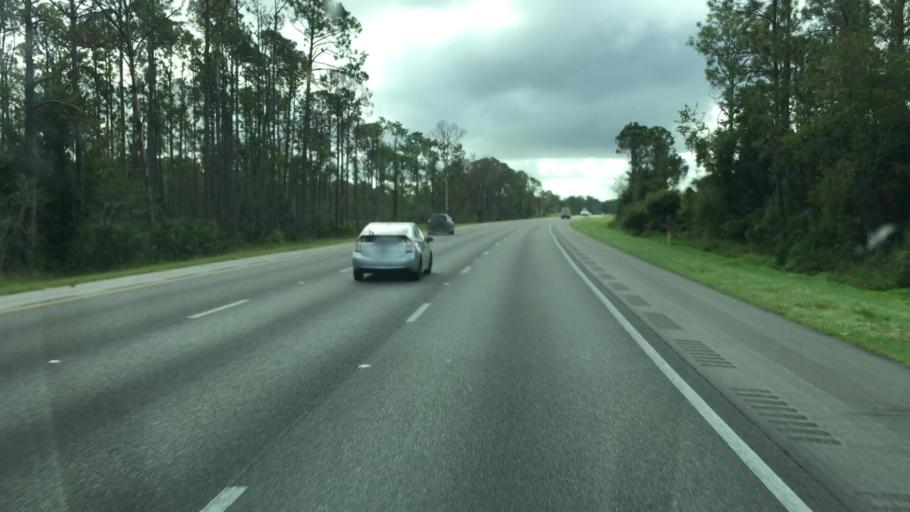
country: US
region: Florida
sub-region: Volusia County
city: Glencoe
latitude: 29.0648
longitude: -81.0093
